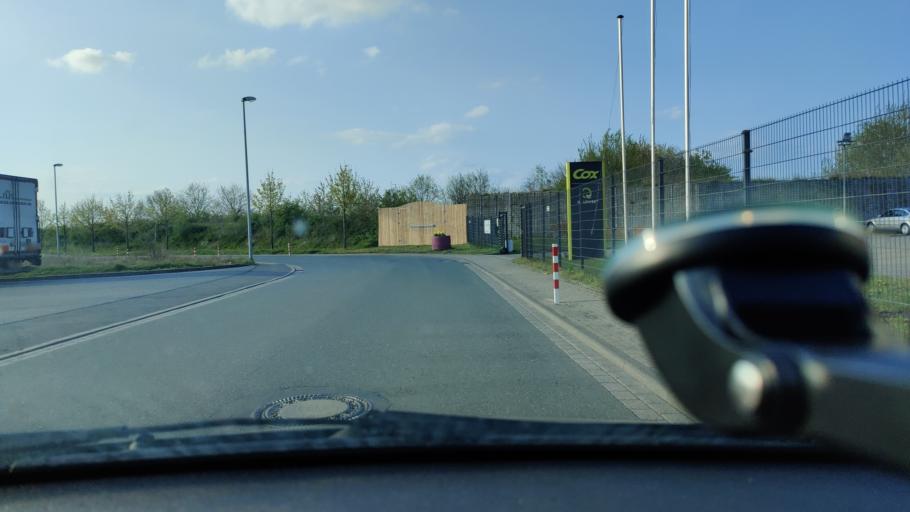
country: DE
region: North Rhine-Westphalia
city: Straelen
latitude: 51.3828
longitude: 6.2461
